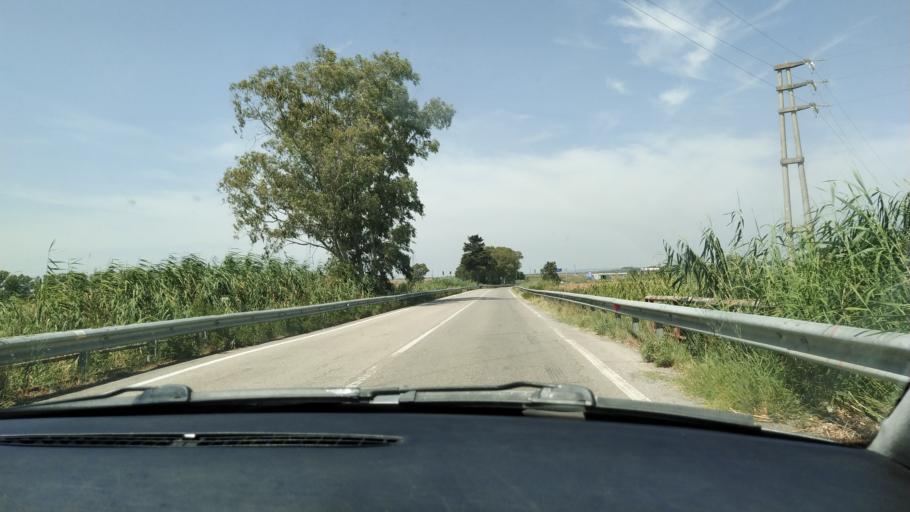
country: IT
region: Apulia
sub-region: Provincia di Taranto
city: Marina di Ginosa
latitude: 40.3754
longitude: 16.7955
